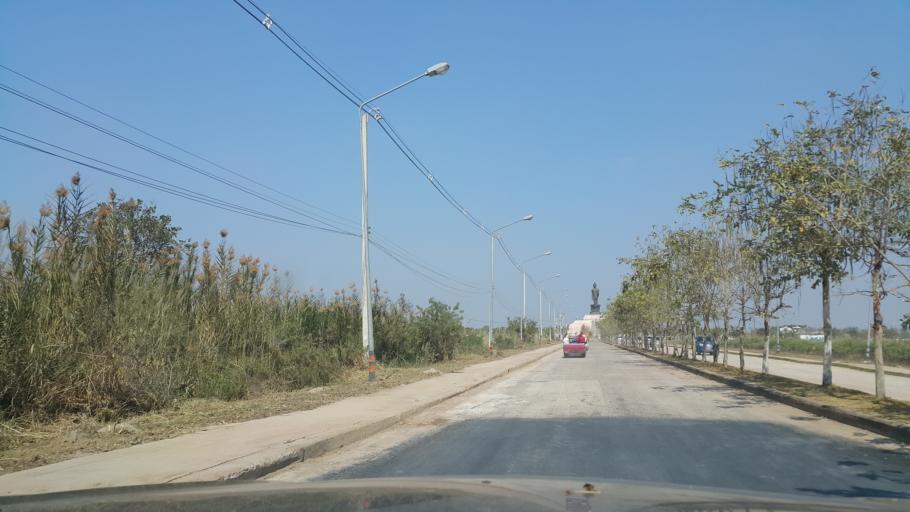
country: TH
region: Khon Kaen
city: Khon Kaen
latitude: 16.5080
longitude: 102.8668
